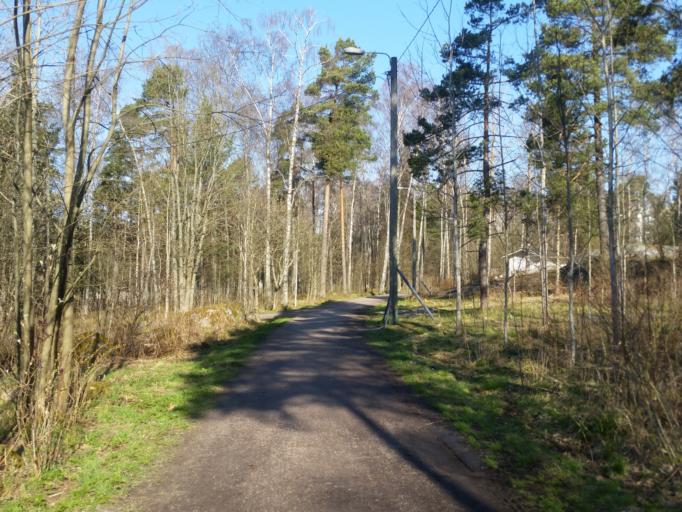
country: FI
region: Uusimaa
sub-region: Helsinki
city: Helsinki
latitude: 60.1462
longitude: 24.8852
